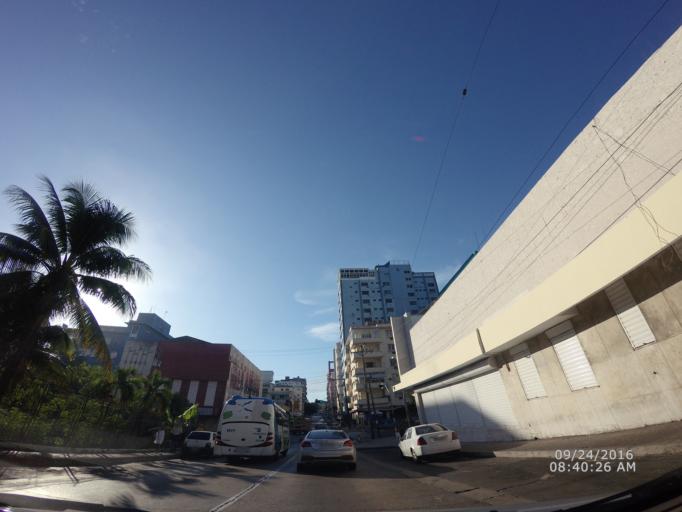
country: CU
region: La Habana
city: Havana
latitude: 23.1420
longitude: -82.3809
